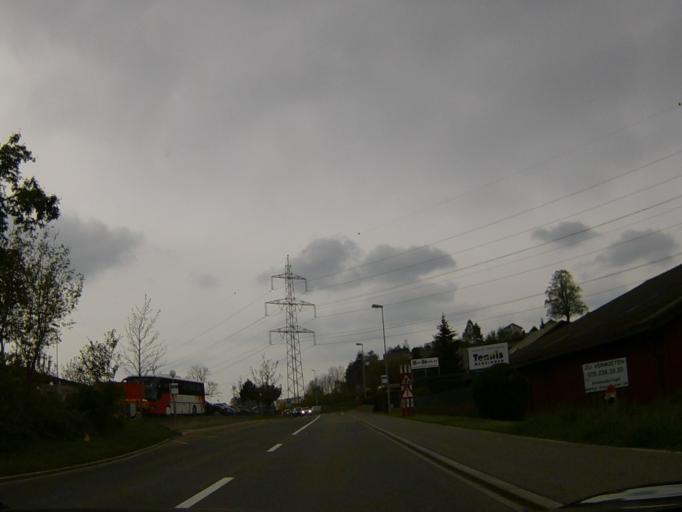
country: CH
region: Zug
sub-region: Zug
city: Menzingen
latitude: 47.1729
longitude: 8.6011
